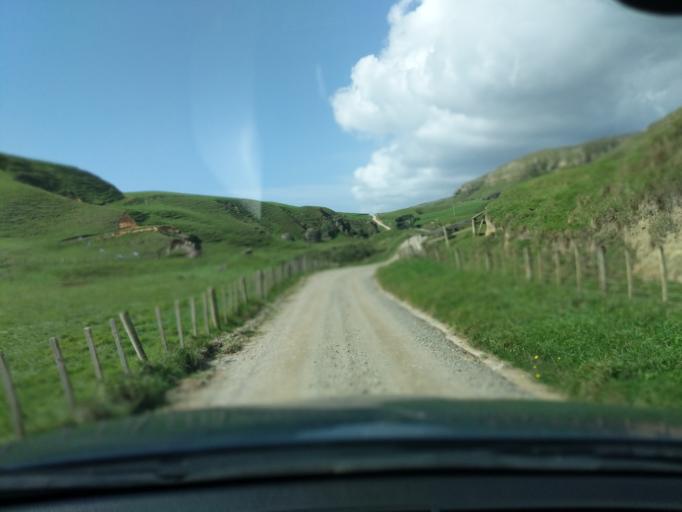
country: NZ
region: Tasman
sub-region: Tasman District
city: Takaka
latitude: -40.6531
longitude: 172.4190
